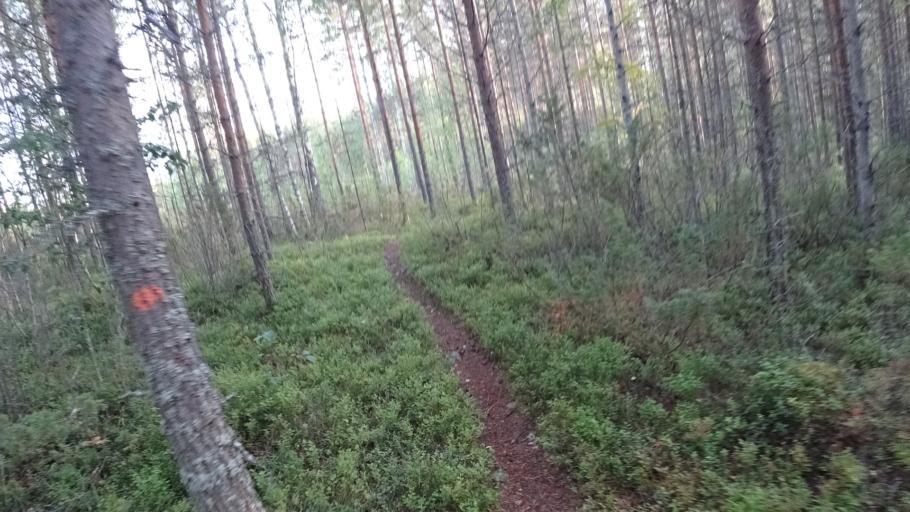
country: FI
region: North Karelia
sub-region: Joensuu
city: Ilomantsi
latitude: 62.6370
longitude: 31.0787
